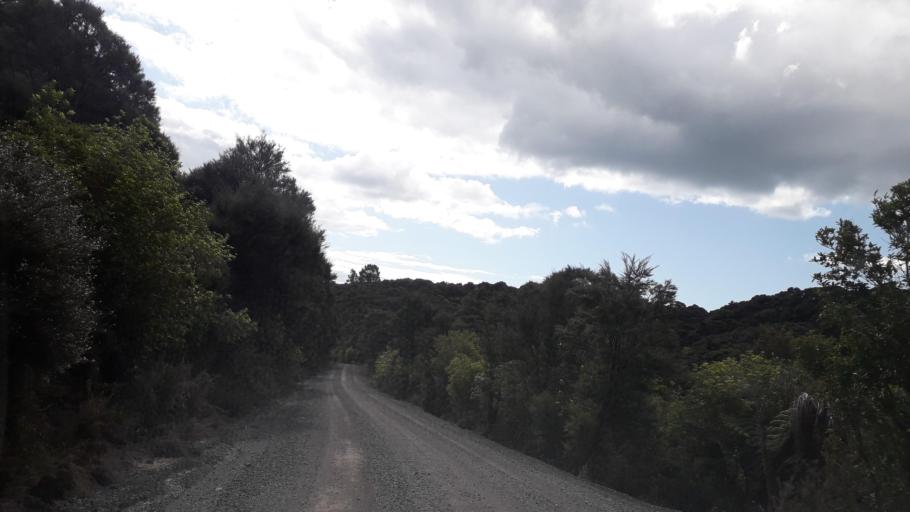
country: NZ
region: Northland
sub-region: Far North District
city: Paihia
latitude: -35.3030
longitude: 174.2217
